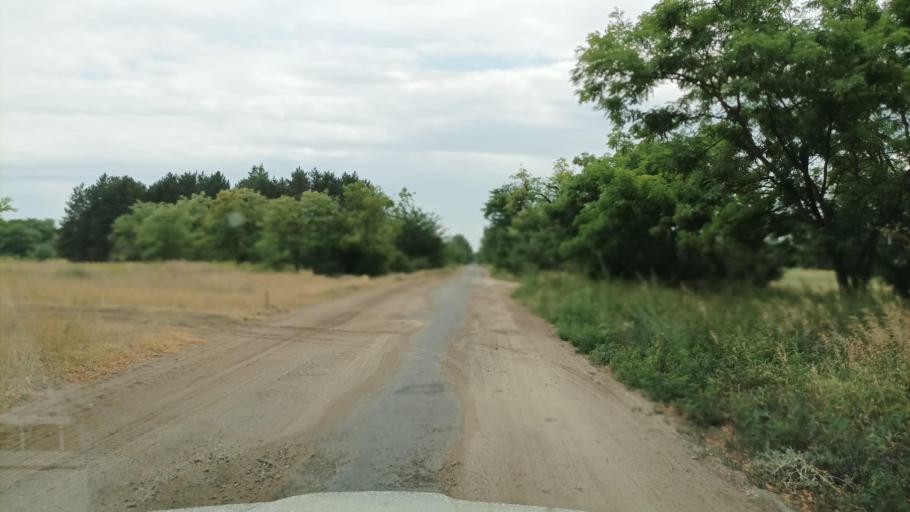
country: HU
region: Pest
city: Orkeny
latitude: 47.0314
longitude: 19.3618
